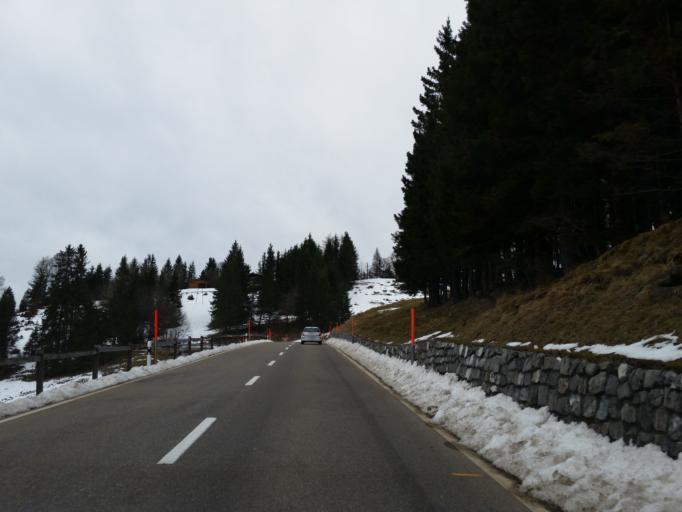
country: CH
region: Appenzell Ausserrhoden
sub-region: Bezirk Hinterland
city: Urnasch
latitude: 47.2665
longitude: 9.2990
